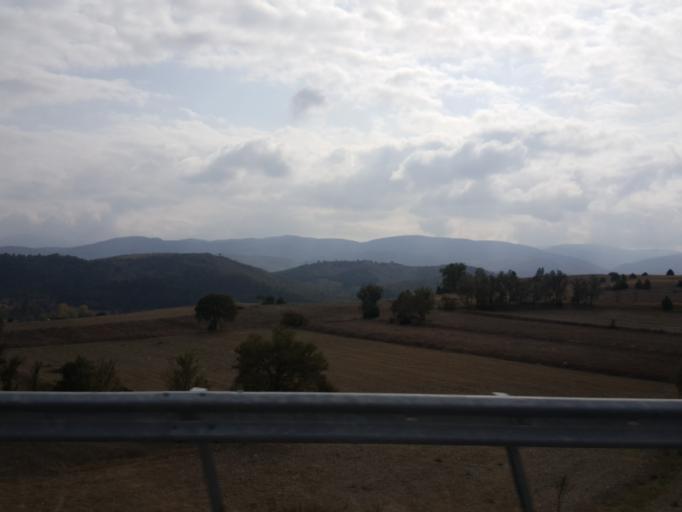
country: TR
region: Sinop
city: Sarayduzu
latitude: 41.3444
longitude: 34.8197
